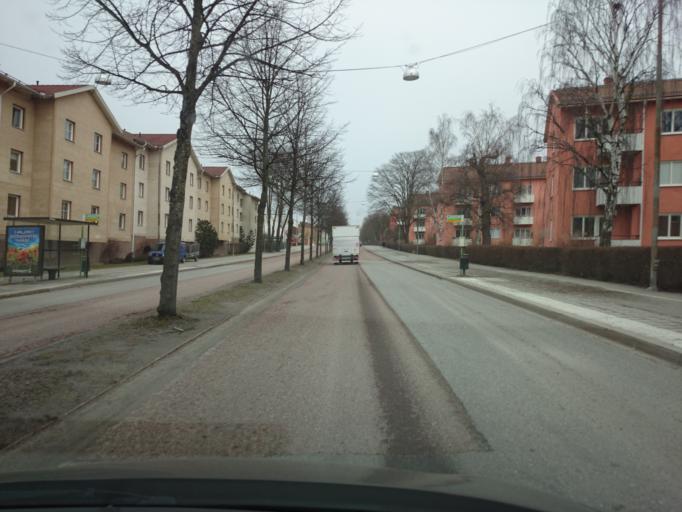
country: SE
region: Uppsala
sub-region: Uppsala Kommun
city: Uppsala
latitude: 59.8730
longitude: 17.6260
